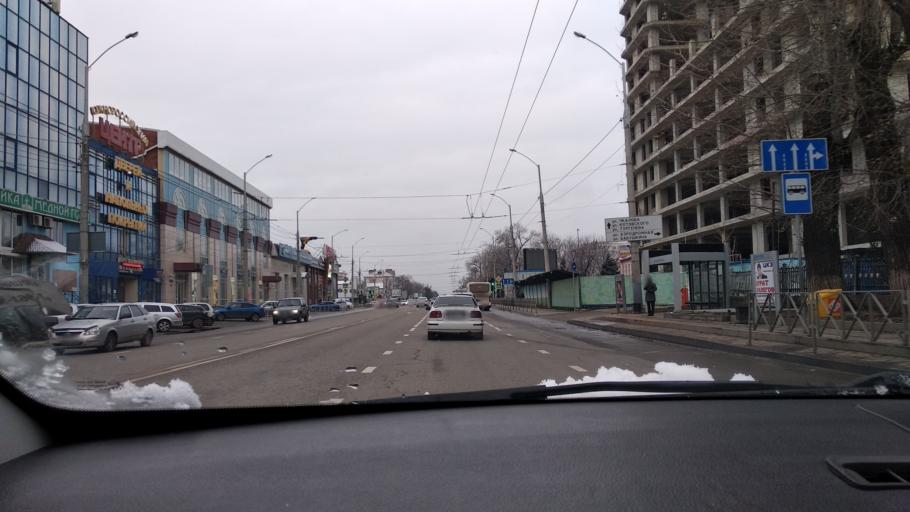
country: RU
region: Krasnodarskiy
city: Krasnodar
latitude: 45.0412
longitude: 38.9691
